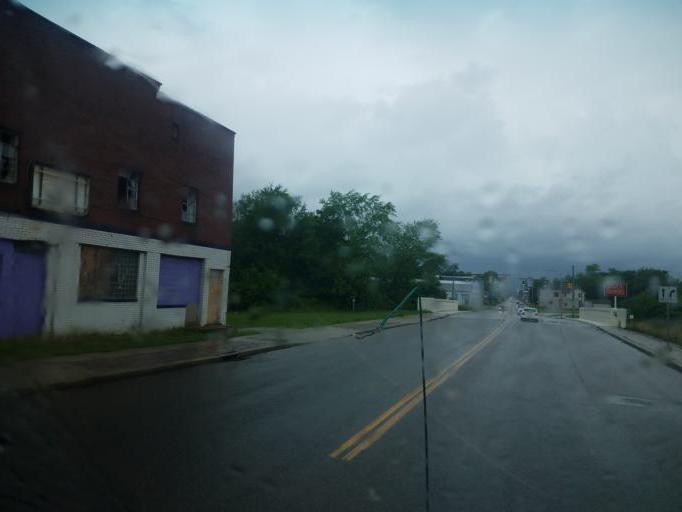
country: US
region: Ohio
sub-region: Stark County
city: Canton
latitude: 40.7949
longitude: -81.3571
